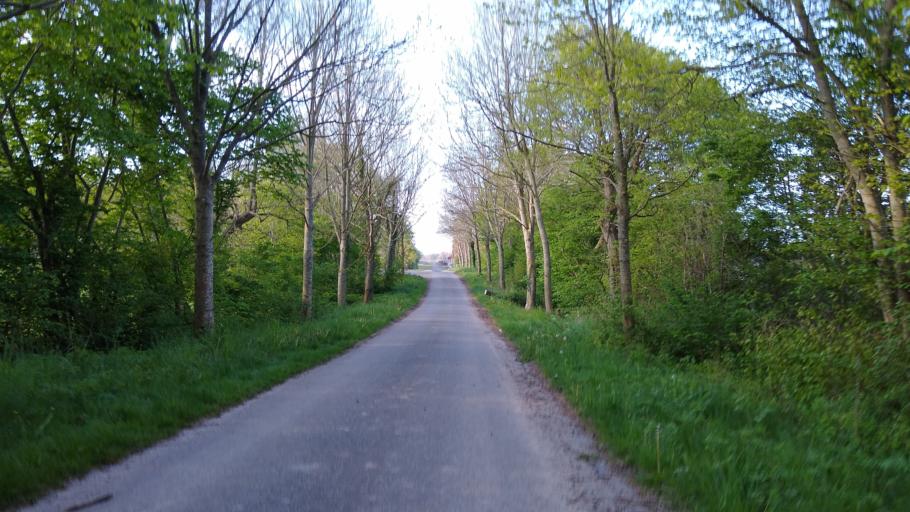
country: DK
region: South Denmark
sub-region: Fredericia Kommune
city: Snoghoj
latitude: 55.5696
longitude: 9.6943
